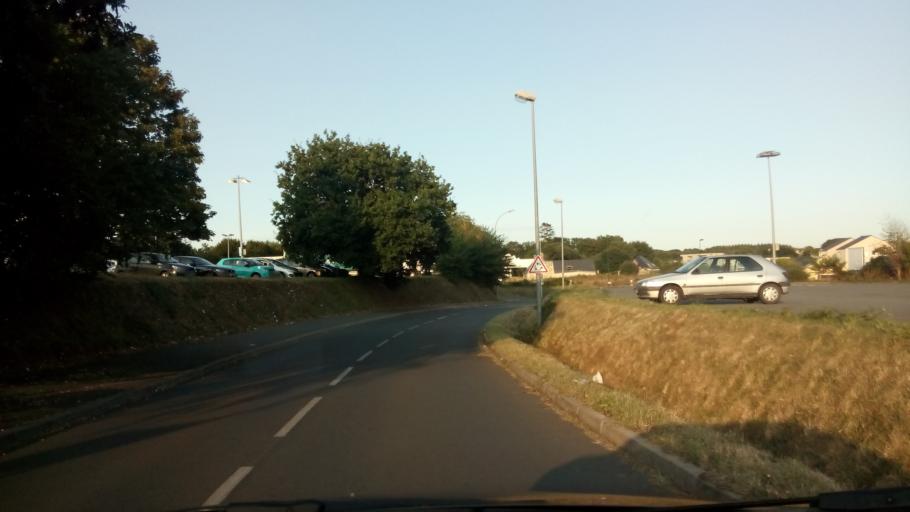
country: FR
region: Brittany
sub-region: Departement des Cotes-d'Armor
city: Lannion
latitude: 48.7481
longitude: -3.4589
